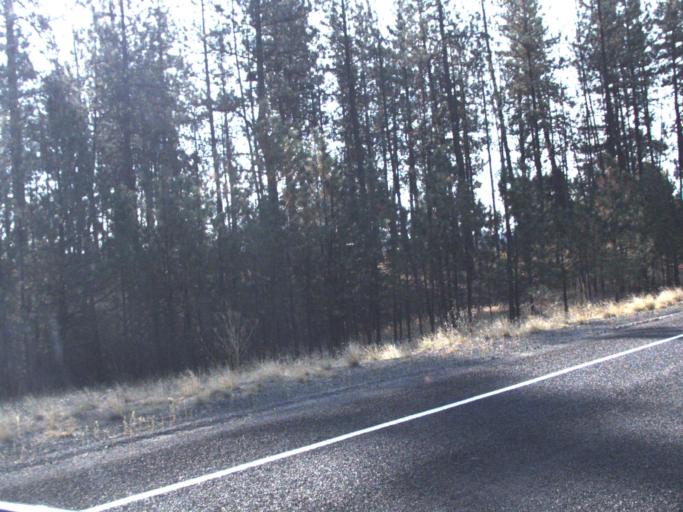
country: US
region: Washington
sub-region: Spokane County
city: Deer Park
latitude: 47.8694
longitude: -117.7062
